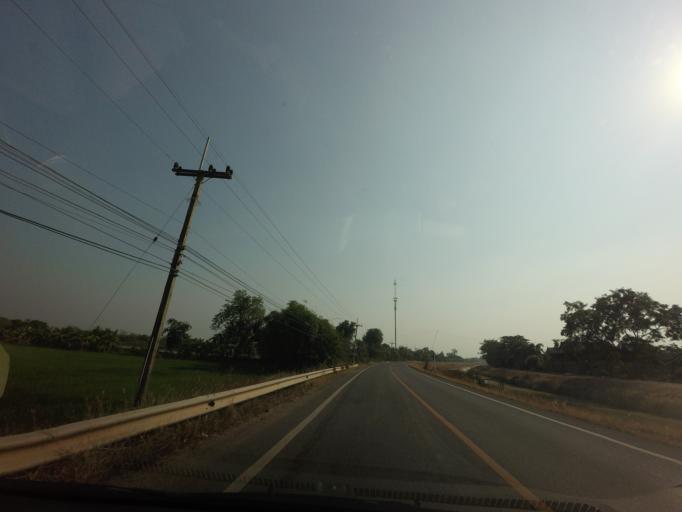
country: TH
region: Chachoengsao
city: Khlong Khuean
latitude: 13.7977
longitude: 101.1778
